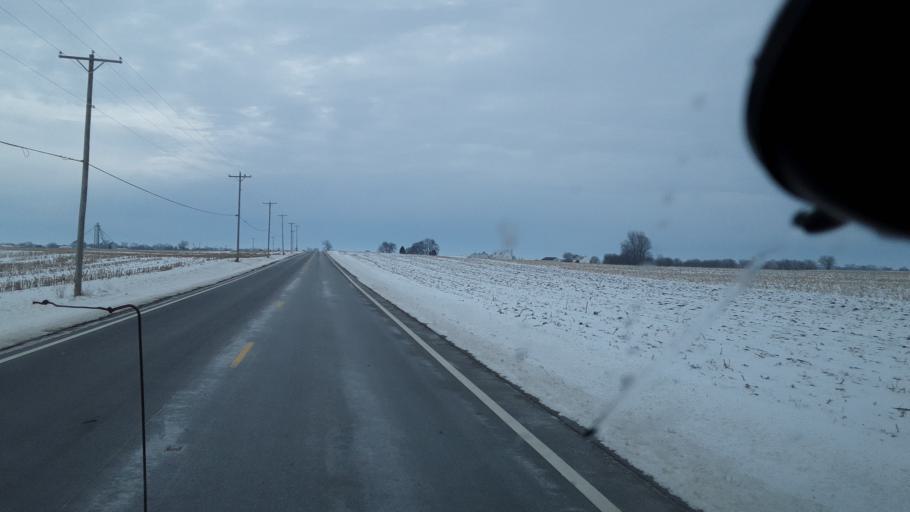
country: US
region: Ohio
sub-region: Madison County
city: Bethel
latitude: 39.7509
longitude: -83.4814
